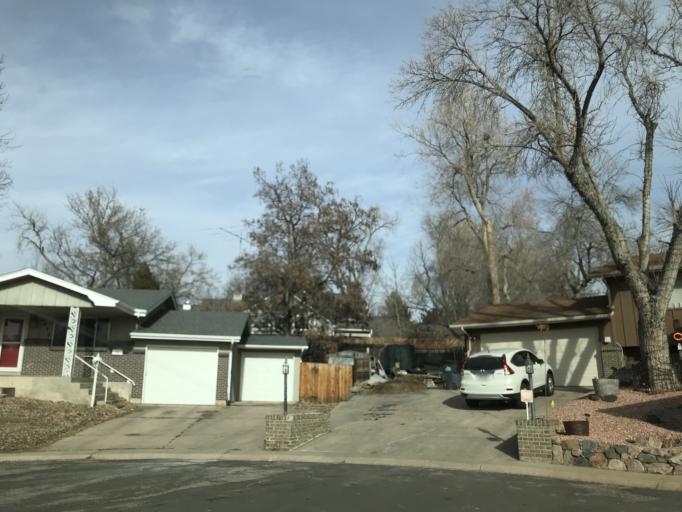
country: US
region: Colorado
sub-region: Arapahoe County
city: Littleton
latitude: 39.6066
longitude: -105.0097
